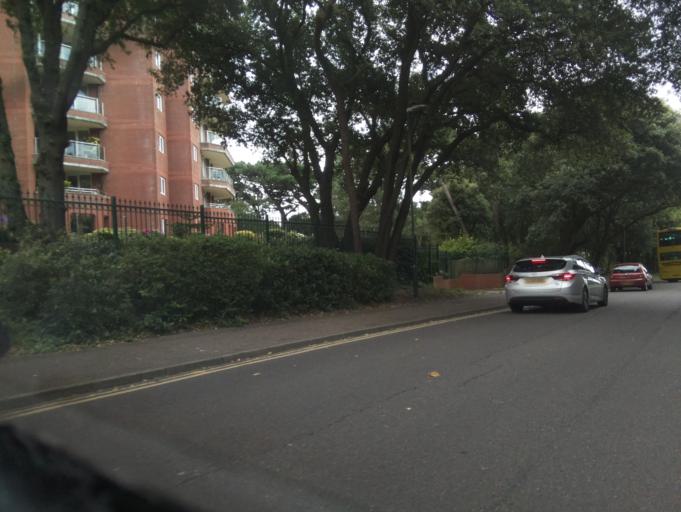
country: GB
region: England
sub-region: Bournemouth
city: Bournemouth
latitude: 50.7214
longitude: -1.8499
